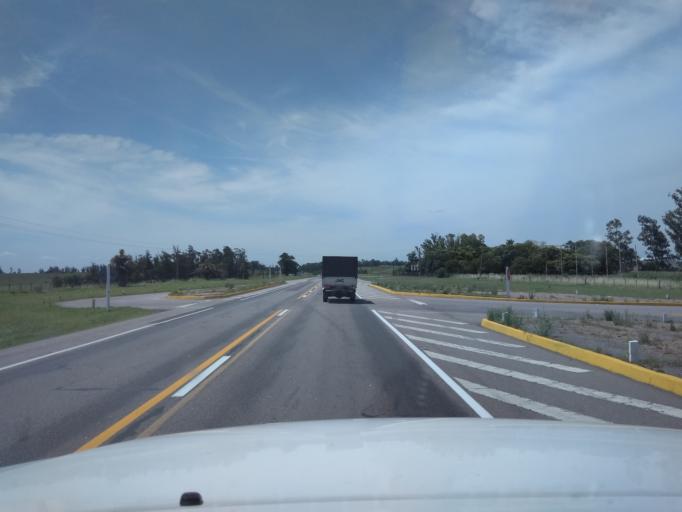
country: UY
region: Florida
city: Florida
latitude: -34.1347
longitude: -56.1838
